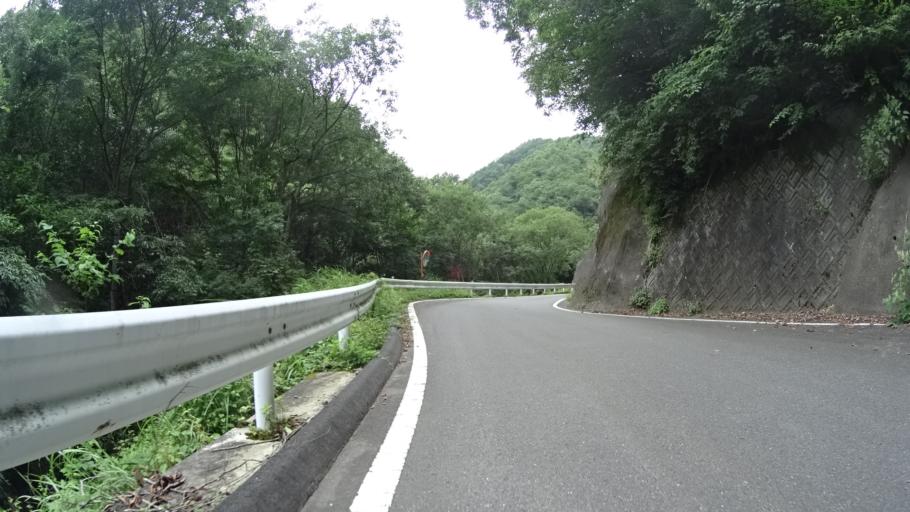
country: JP
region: Nagano
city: Saku
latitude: 36.0648
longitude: 138.6540
